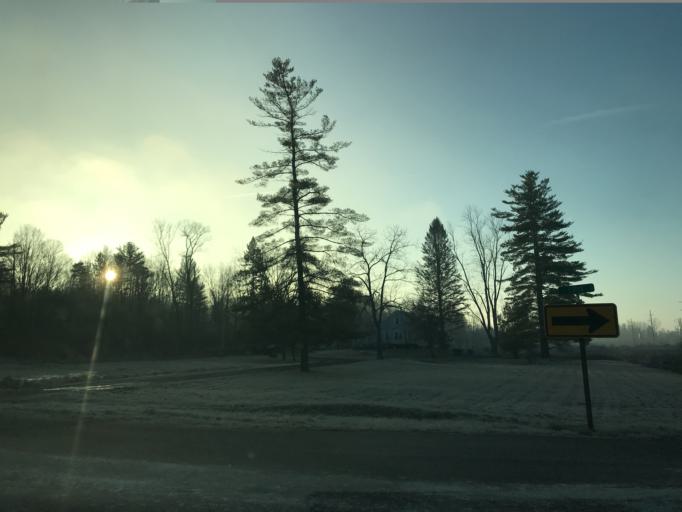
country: US
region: Michigan
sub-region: Ingham County
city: Leslie
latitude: 42.3825
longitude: -84.4623
